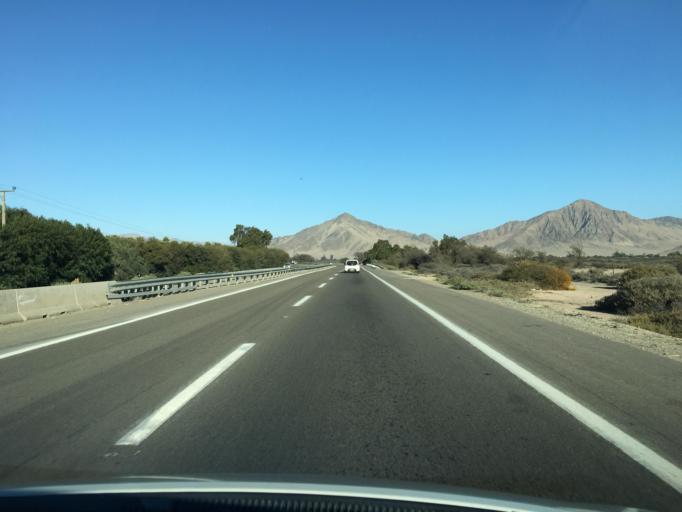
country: CL
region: Atacama
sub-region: Provincia de Copiapo
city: Copiapo
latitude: -27.2980
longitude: -70.4585
